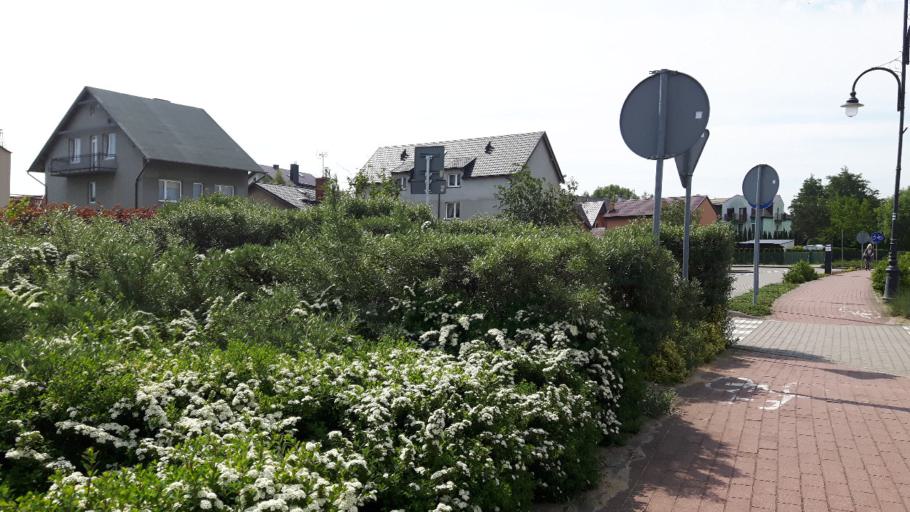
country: PL
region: Pomeranian Voivodeship
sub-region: Powiat leborski
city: Leba
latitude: 54.7523
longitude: 17.5631
